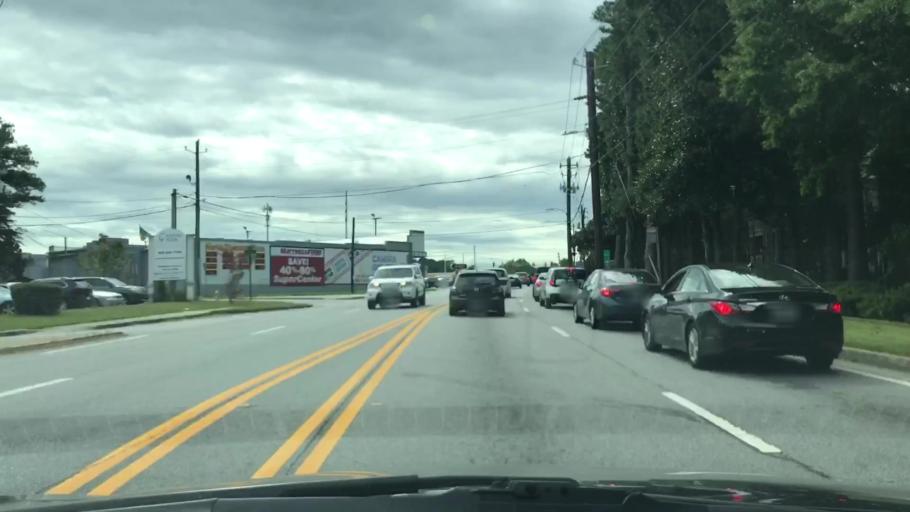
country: US
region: Georgia
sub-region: DeKalb County
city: North Decatur
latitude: 33.7922
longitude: -84.3058
